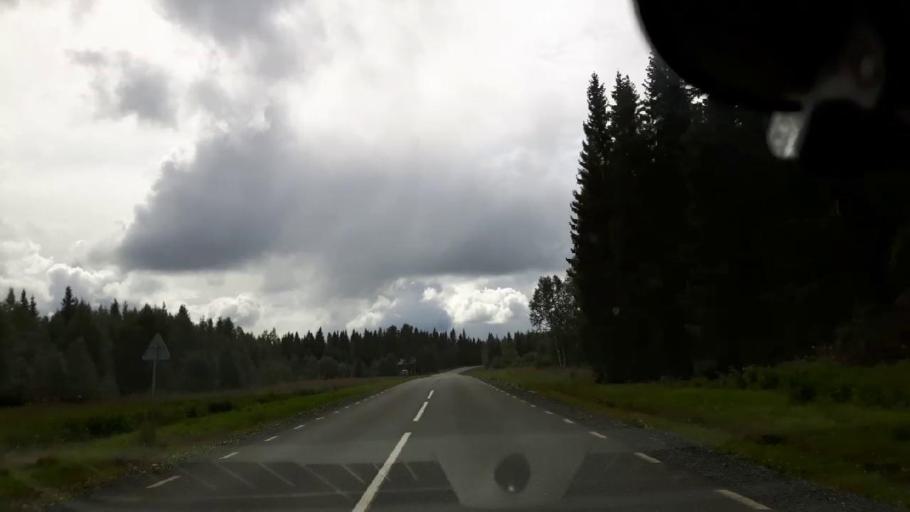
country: SE
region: Jaemtland
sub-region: Krokoms Kommun
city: Valla
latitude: 63.4801
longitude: 13.8563
